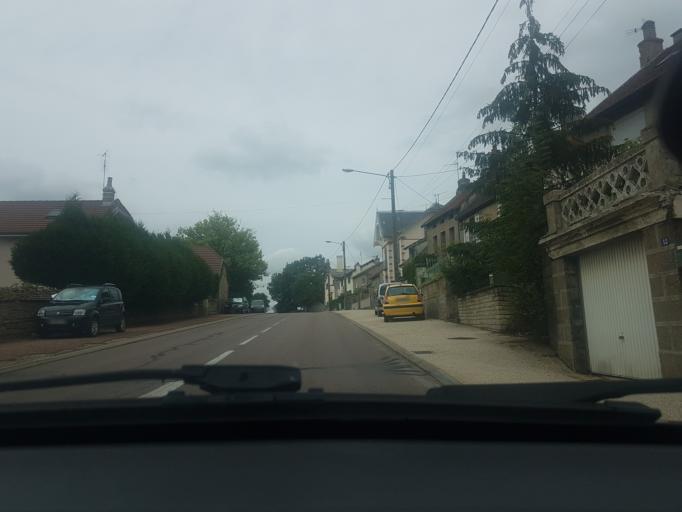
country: FR
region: Bourgogne
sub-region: Departement de la Cote-d'Or
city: Arnay-le-Duc
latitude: 47.1366
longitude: 4.4839
